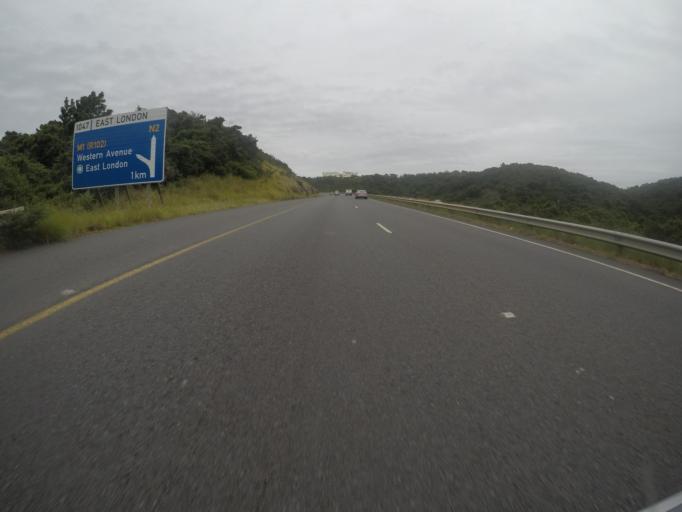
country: ZA
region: Eastern Cape
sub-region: Buffalo City Metropolitan Municipality
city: East London
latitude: -32.9703
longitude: 27.9095
